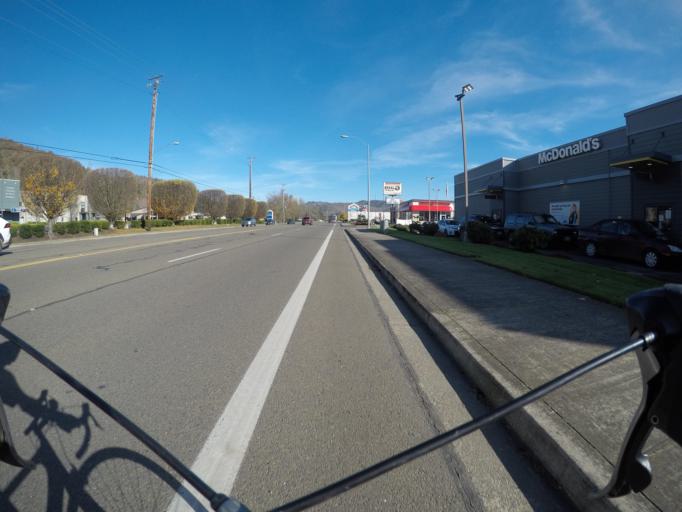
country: US
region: Oregon
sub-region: Douglas County
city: Roseburg
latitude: 43.2380
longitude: -123.3699
